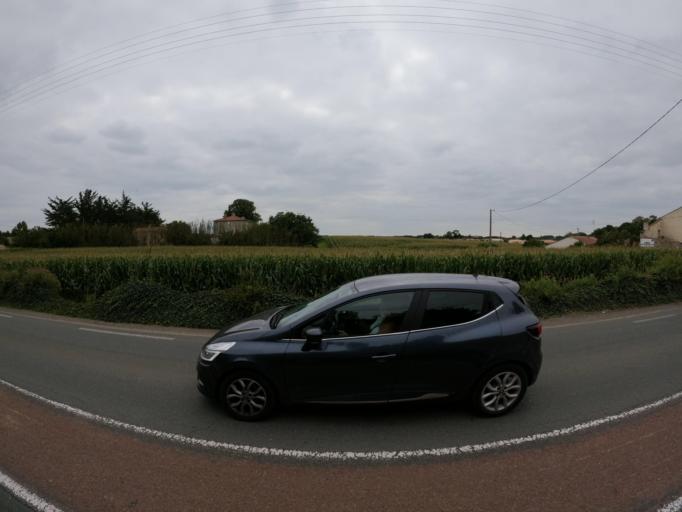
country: FR
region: Pays de la Loire
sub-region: Departement de la Vendee
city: Benet
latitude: 46.3985
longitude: -0.6594
